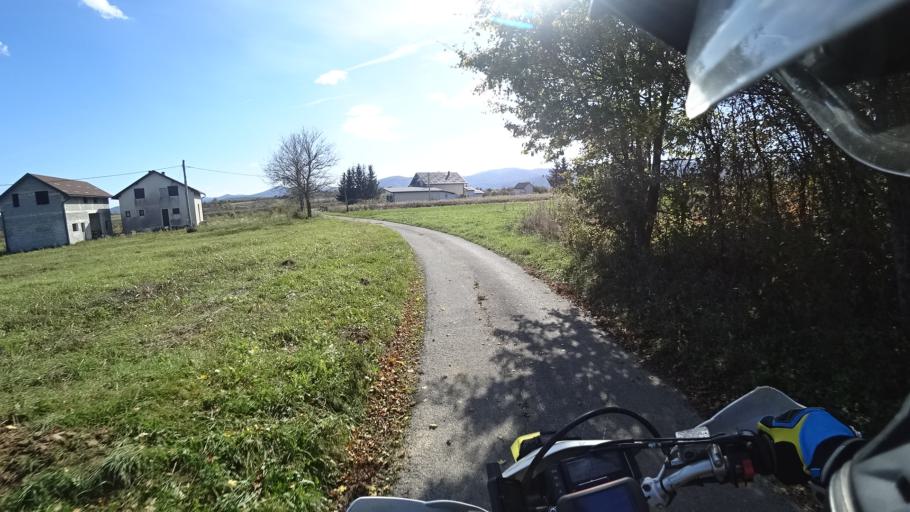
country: HR
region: Karlovacka
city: Plaski
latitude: 45.1096
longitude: 15.3596
